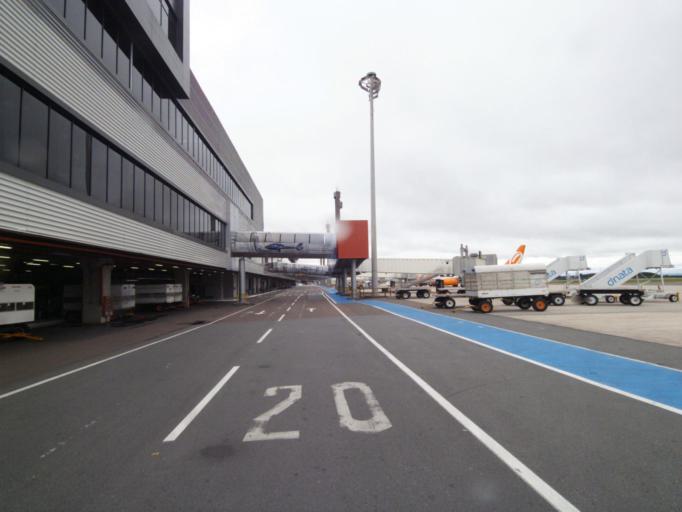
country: BR
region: Parana
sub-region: Sao Jose Dos Pinhais
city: Sao Jose dos Pinhais
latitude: -25.5366
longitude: -49.1716
